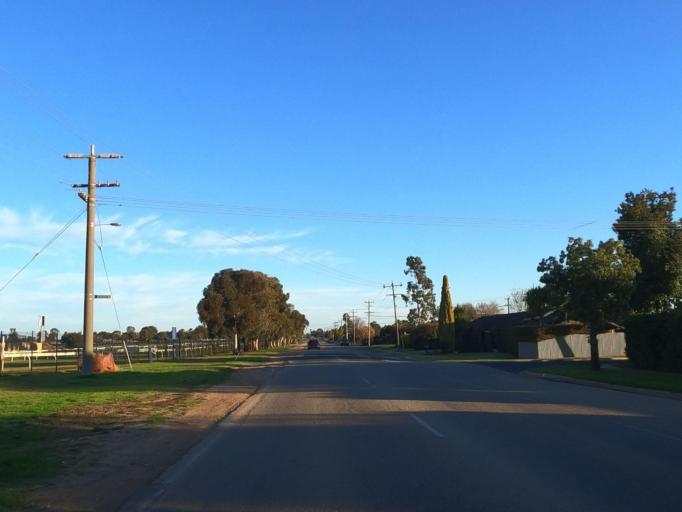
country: AU
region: Victoria
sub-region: Swan Hill
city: Swan Hill
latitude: -35.3490
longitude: 143.5549
